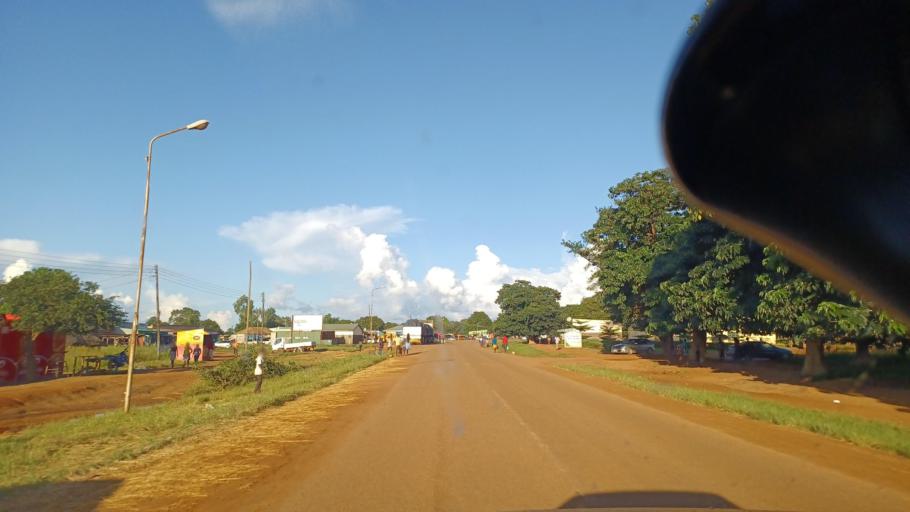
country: ZM
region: North-Western
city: Kalengwa
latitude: -13.1370
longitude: 25.0053
